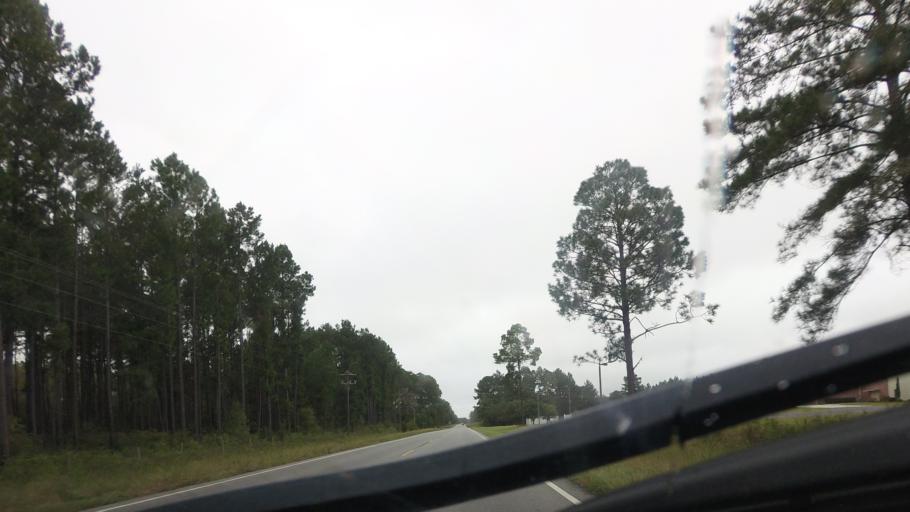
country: US
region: Georgia
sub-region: Berrien County
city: Nashville
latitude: 31.2703
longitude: -83.2396
